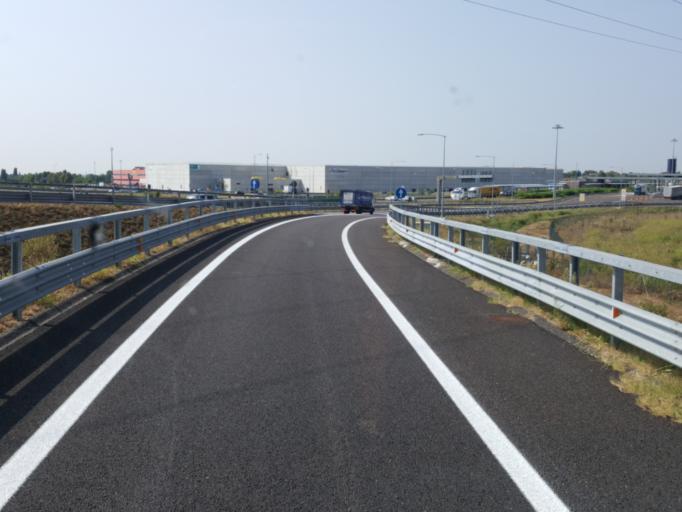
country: IT
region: Lombardy
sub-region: Citta metropolitana di Milano
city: Pozzuolo Martesana
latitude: 45.5182
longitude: 9.4392
